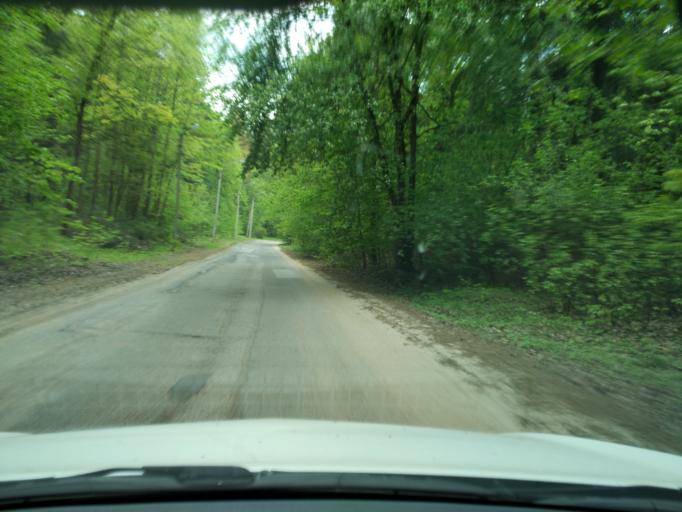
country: LT
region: Vilnius County
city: Rasos
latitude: 54.6962
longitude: 25.3240
